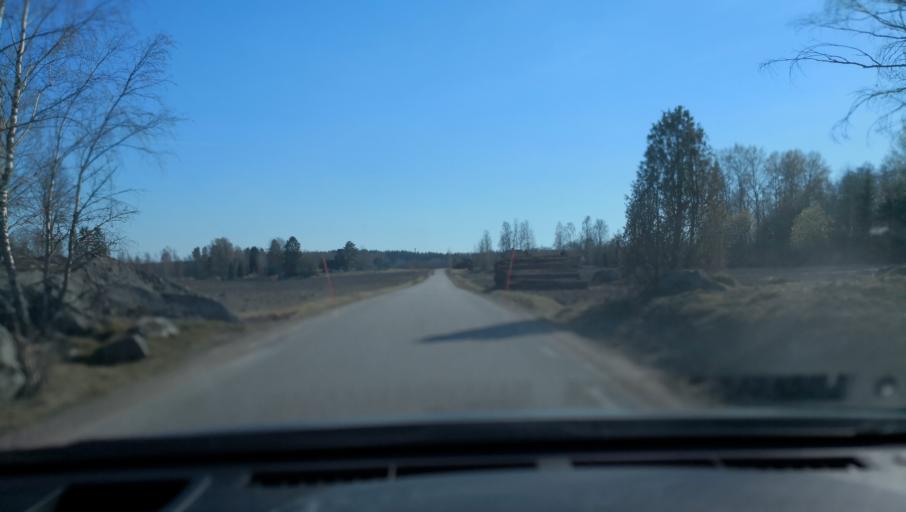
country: SE
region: Vaestmanland
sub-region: Sala Kommun
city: Sala
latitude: 60.0818
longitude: 16.4971
